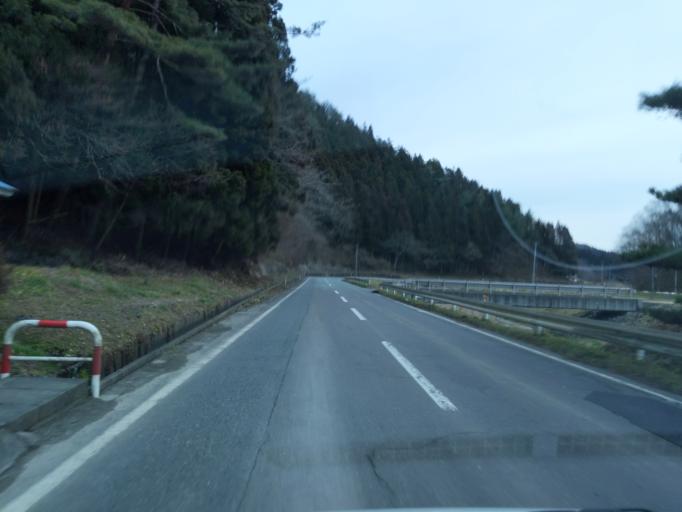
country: JP
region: Iwate
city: Mizusawa
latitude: 39.0510
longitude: 141.2925
